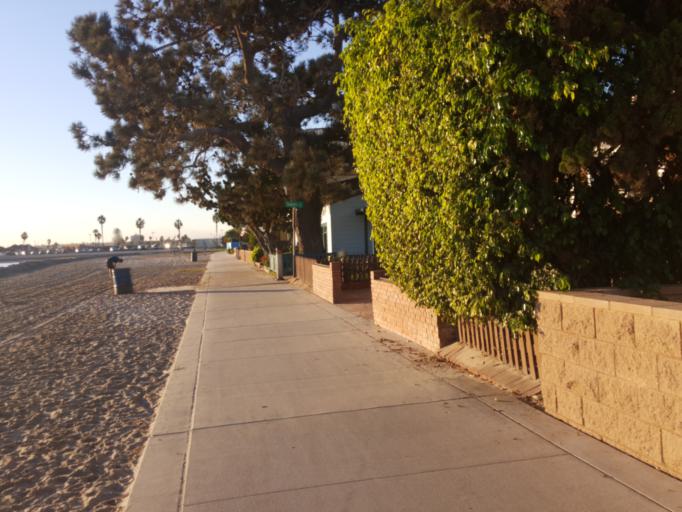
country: US
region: California
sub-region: San Diego County
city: La Jolla
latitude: 32.7855
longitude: -117.2521
